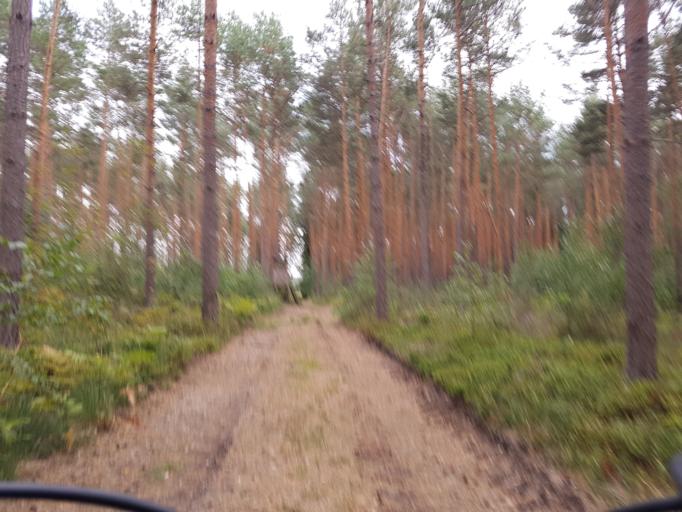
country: DE
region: Brandenburg
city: Trobitz
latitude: 51.5567
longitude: 13.4514
